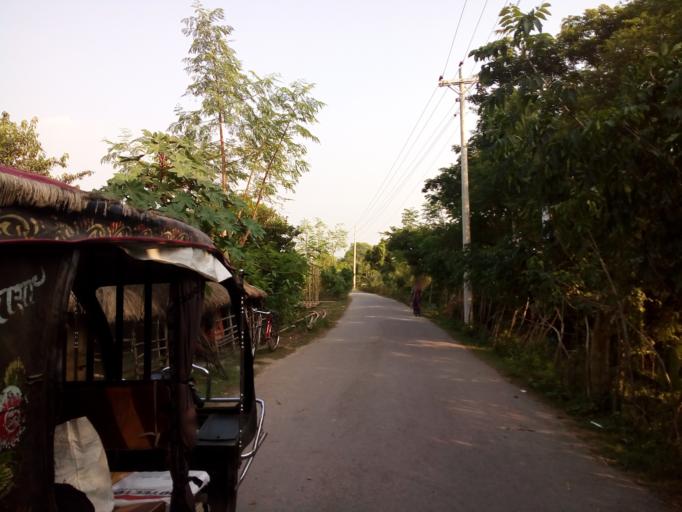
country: BD
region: Khulna
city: Phultala
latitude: 22.7267
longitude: 89.4625
